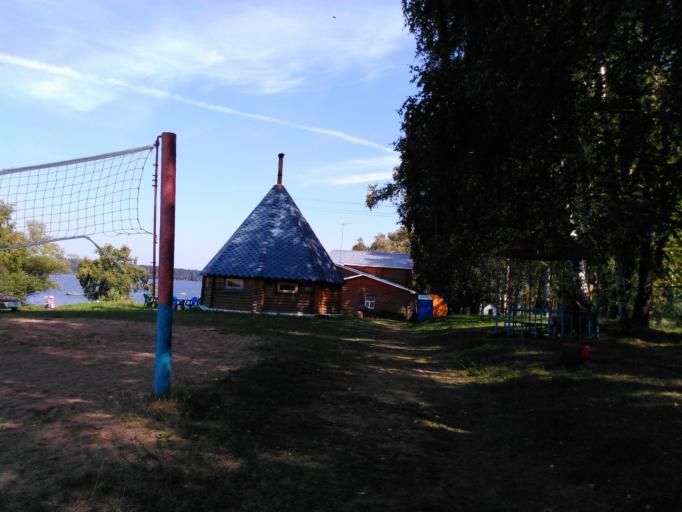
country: RU
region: Tverskaya
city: Konakovo
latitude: 56.6839
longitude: 36.6940
